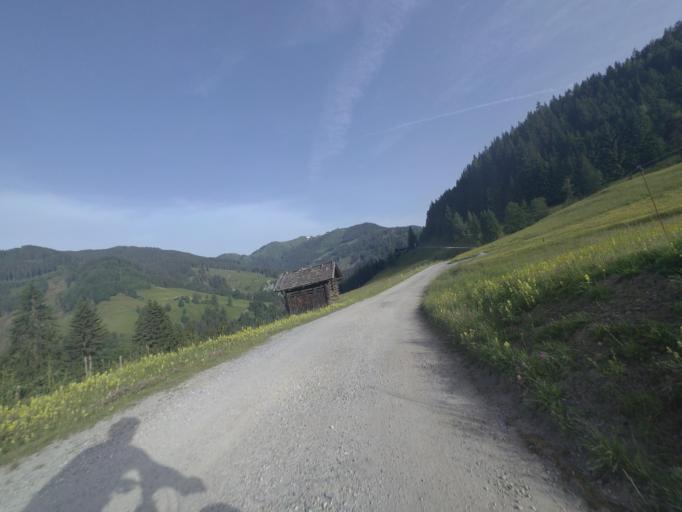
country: AT
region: Salzburg
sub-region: Politischer Bezirk Sankt Johann im Pongau
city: Muhlbach am Hochkonig
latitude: 47.3557
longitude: 13.1181
